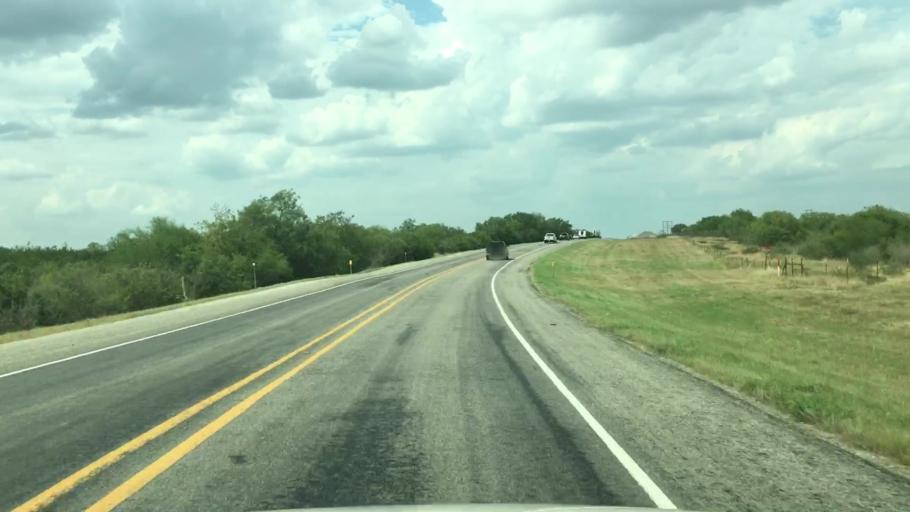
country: US
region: Texas
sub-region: Live Oak County
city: Three Rivers
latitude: 28.6433
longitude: -98.2841
